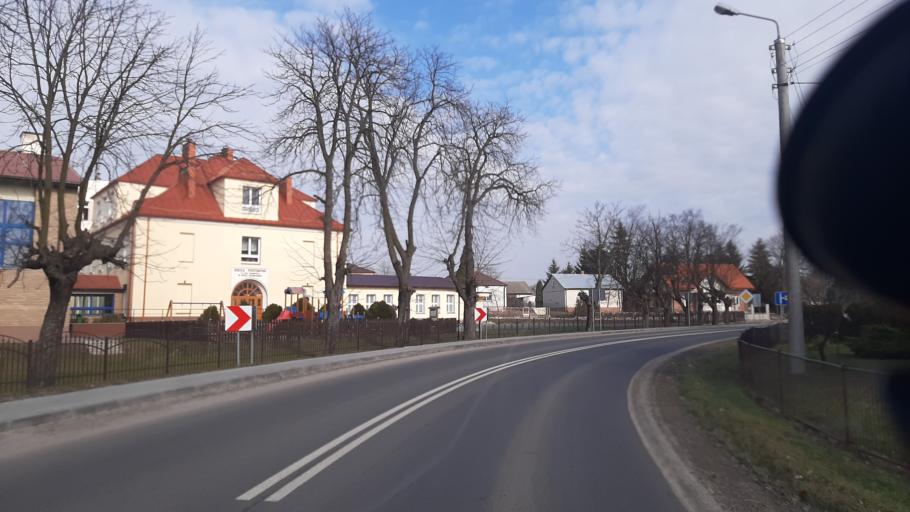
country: PL
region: Lublin Voivodeship
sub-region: Powiat lubartowski
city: Wola Sernicka
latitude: 51.4528
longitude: 22.6724
